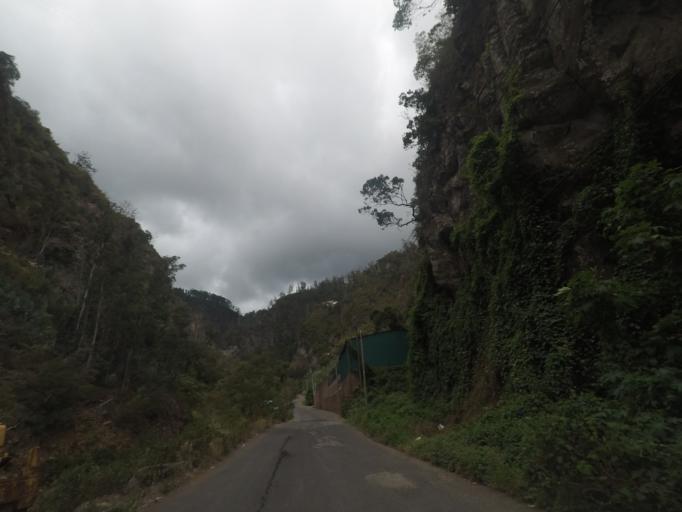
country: PT
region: Madeira
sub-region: Funchal
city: Nossa Senhora do Monte
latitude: 32.6790
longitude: -16.9174
